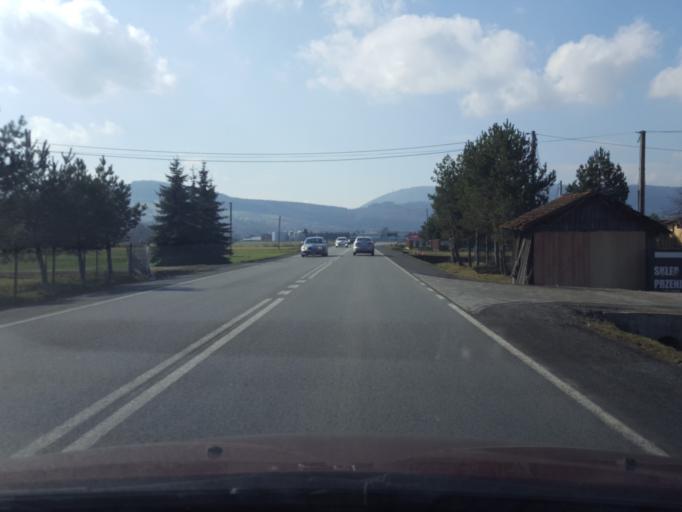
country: PL
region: Lesser Poland Voivodeship
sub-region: Powiat nowosadecki
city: Lososina Dolna
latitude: 49.7507
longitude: 20.6327
